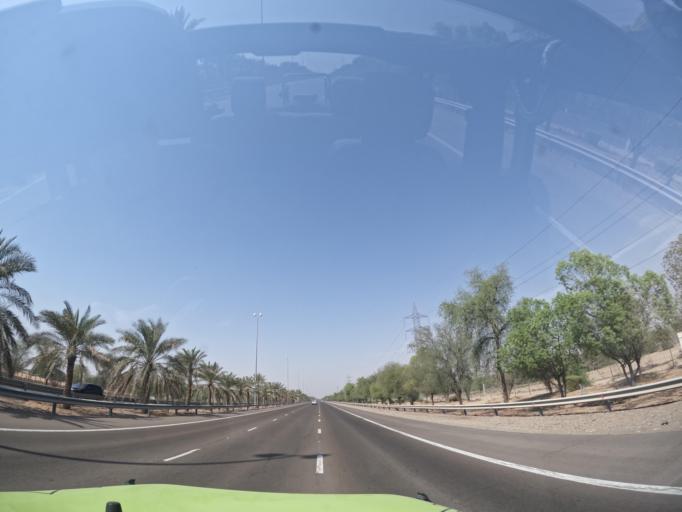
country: AE
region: Abu Dhabi
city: Al Ain
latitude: 24.2074
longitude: 55.4361
